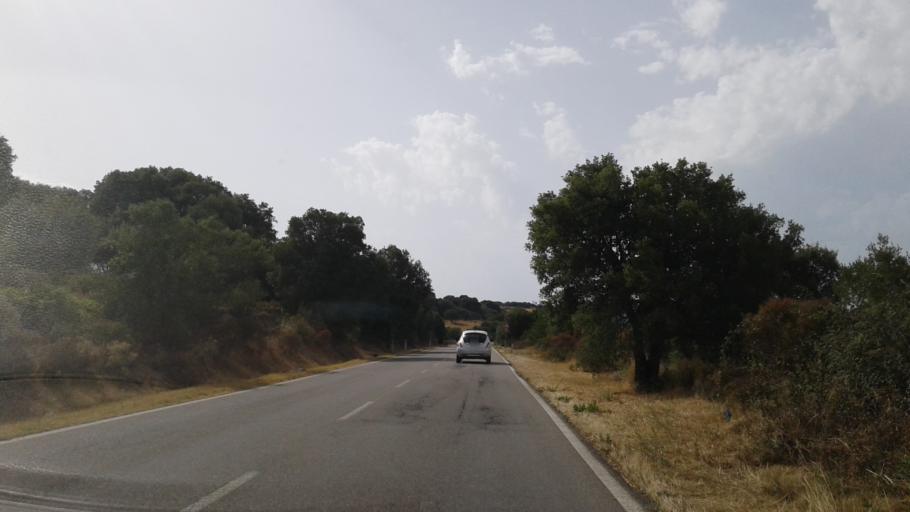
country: IT
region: Sardinia
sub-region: Provincia di Olbia-Tempio
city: Sant'Antonio di Gallura
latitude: 40.9702
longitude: 9.2726
